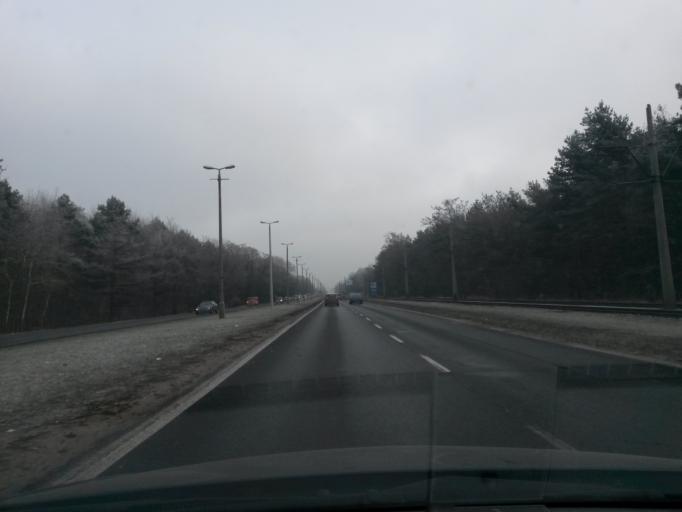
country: PL
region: Greater Poland Voivodeship
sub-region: Powiat poznanski
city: Czerwonak
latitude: 52.4101
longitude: 16.9980
